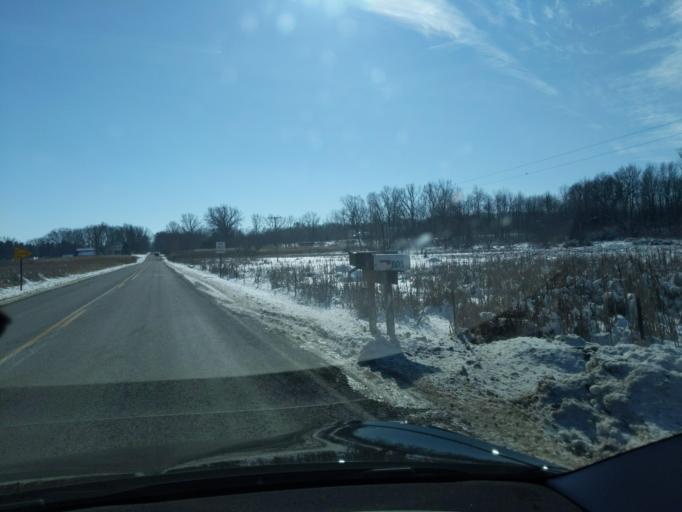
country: US
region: Michigan
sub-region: Livingston County
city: Fowlerville
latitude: 42.5859
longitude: -84.0746
